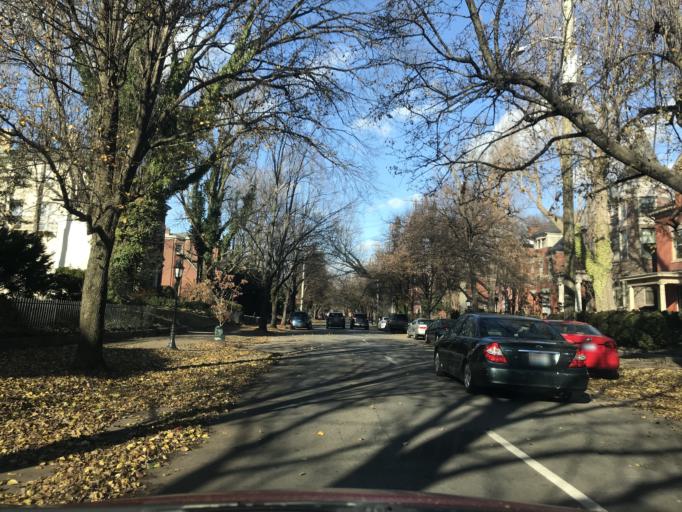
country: US
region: Kentucky
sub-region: Jefferson County
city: Louisville
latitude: 38.2298
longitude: -85.7579
